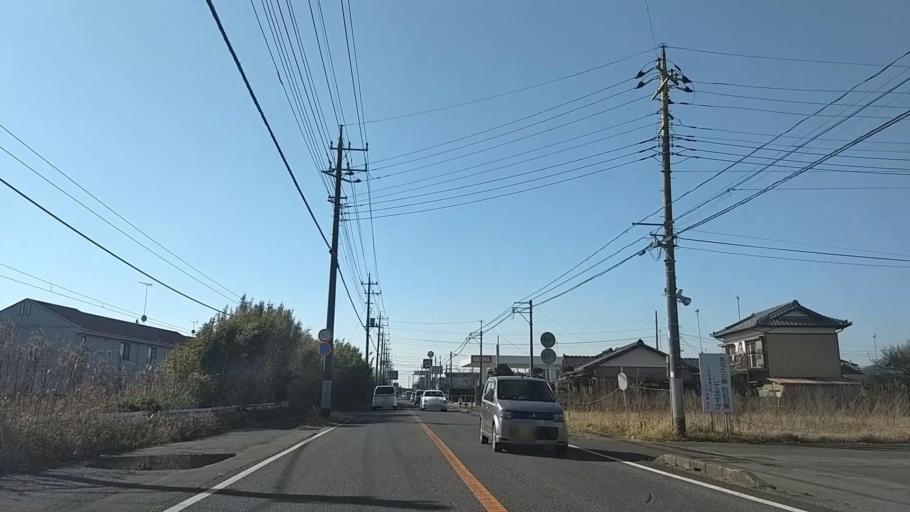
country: JP
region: Chiba
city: Yokaichiba
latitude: 35.7102
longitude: 140.5731
